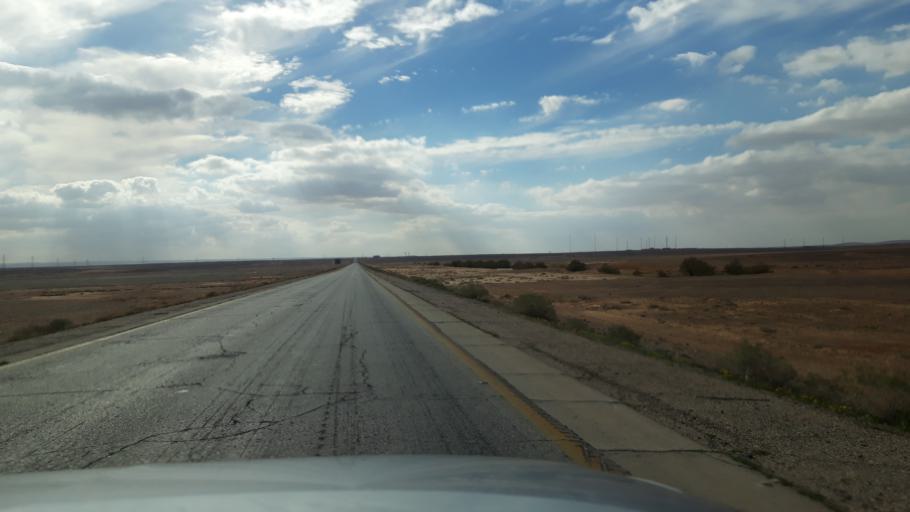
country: JO
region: Amman
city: Al Azraq ash Shamali
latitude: 31.7314
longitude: 36.5036
